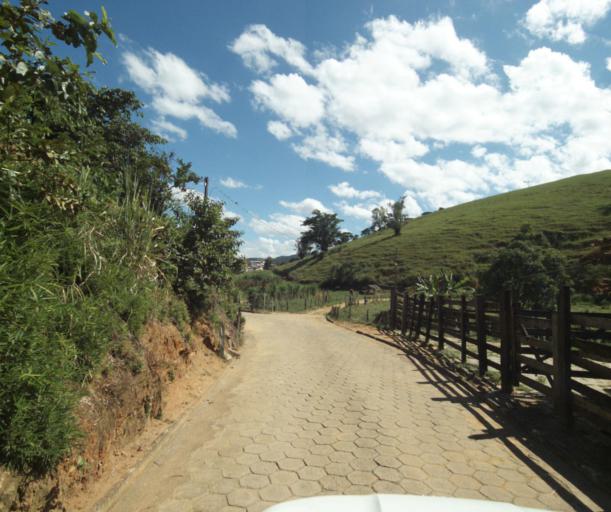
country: BR
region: Espirito Santo
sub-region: Sao Jose Do Calcado
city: Sao Jose do Calcado
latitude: -21.0226
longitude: -41.6564
